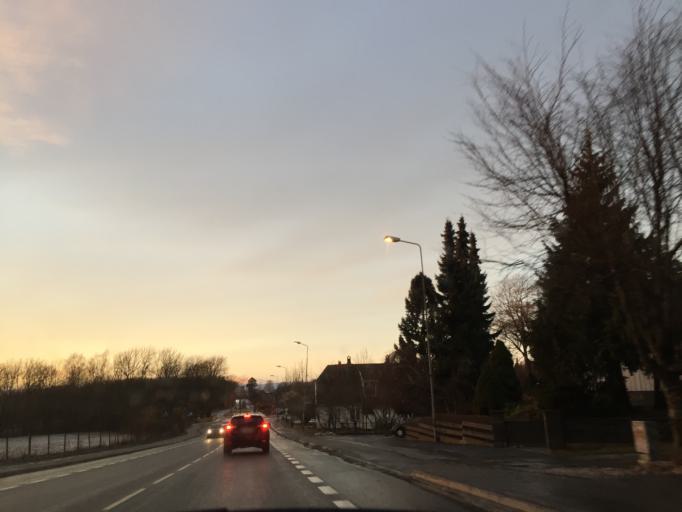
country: NO
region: Ostfold
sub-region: Moss
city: Moss
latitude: 59.4355
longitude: 10.6250
